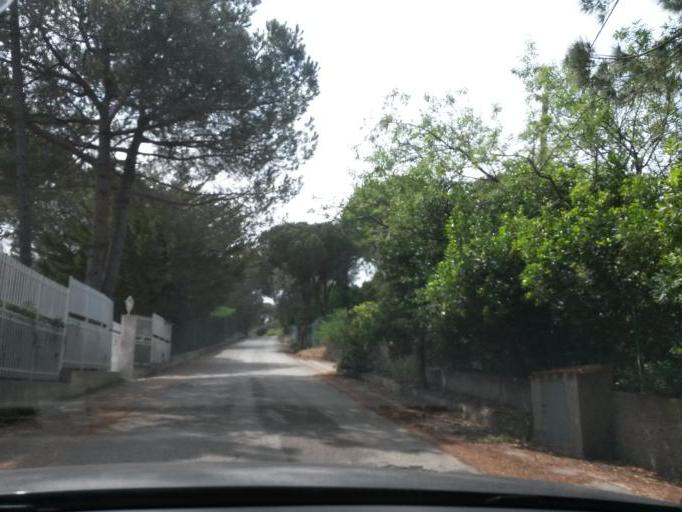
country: IT
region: Tuscany
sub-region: Provincia di Livorno
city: Porto Azzurro
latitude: 42.7508
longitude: 10.4058
